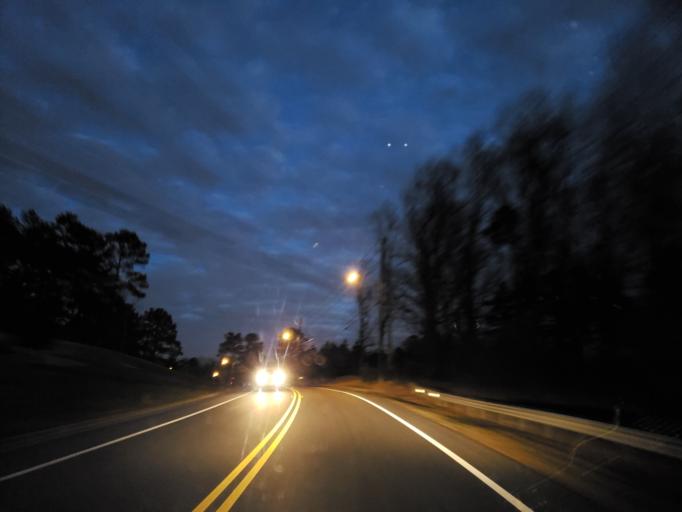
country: US
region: Georgia
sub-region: Cobb County
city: Kennesaw
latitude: 33.9948
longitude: -84.6403
